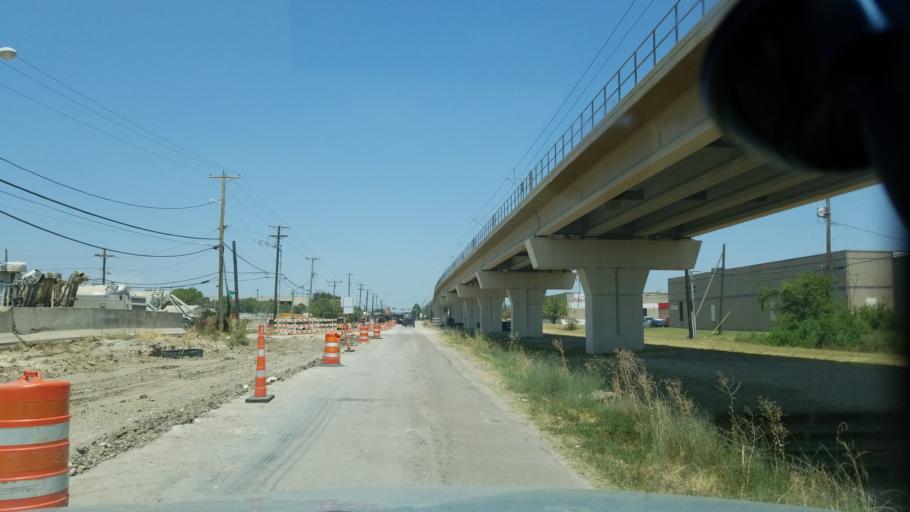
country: US
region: Texas
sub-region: Dallas County
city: Farmers Branch
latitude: 32.8922
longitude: -96.8873
